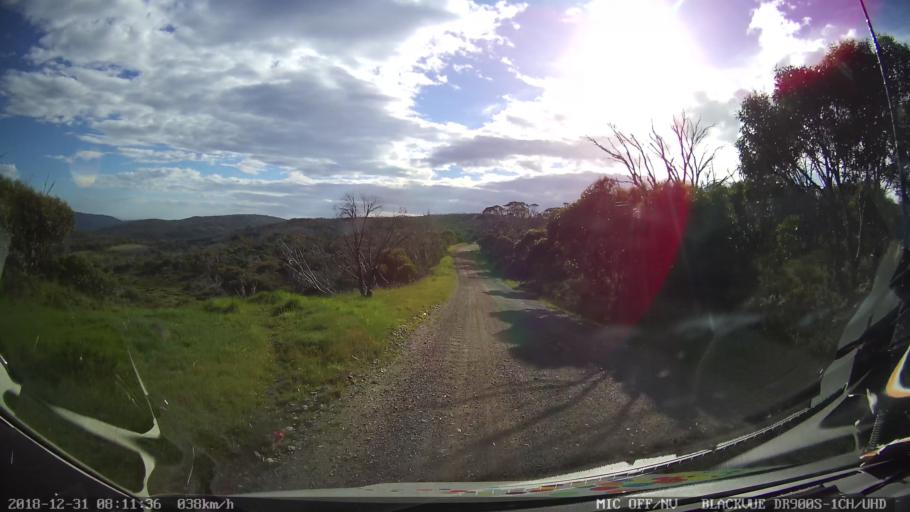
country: AU
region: New South Wales
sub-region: Snowy River
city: Jindabyne
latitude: -36.3856
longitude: 148.4274
